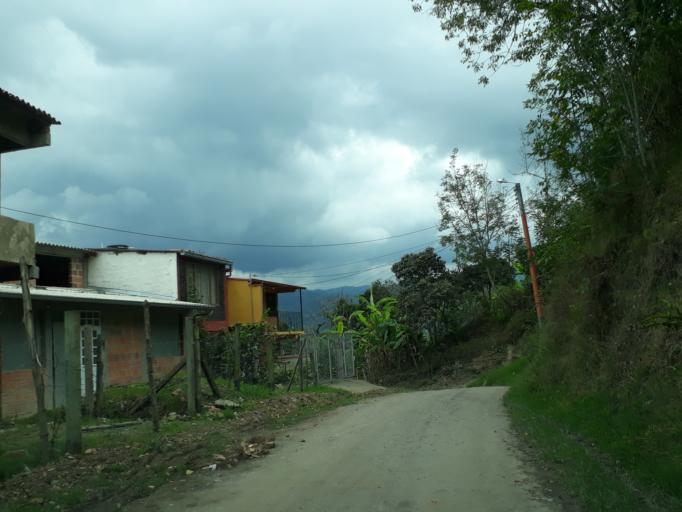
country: CO
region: Cundinamarca
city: Manta
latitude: 5.0114
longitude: -73.5411
